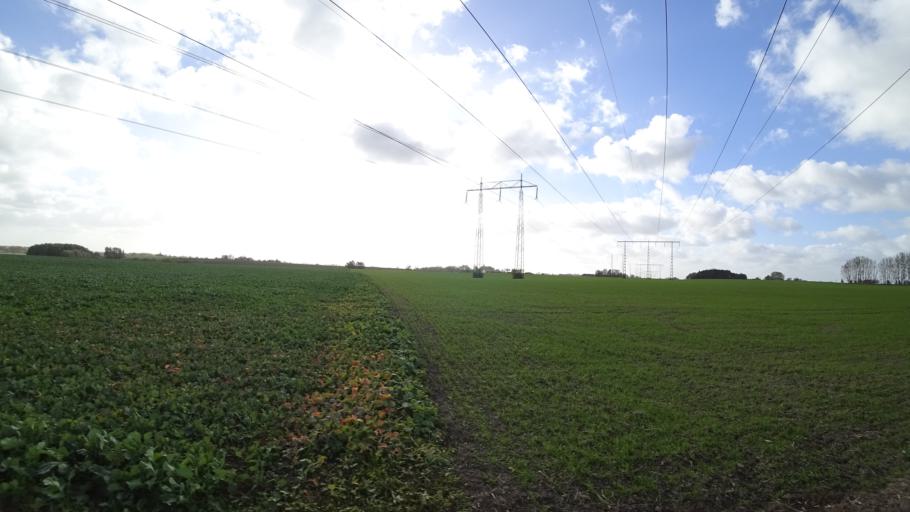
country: SE
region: Skane
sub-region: Staffanstorps Kommun
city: Hjaerup
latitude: 55.6380
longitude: 13.1566
